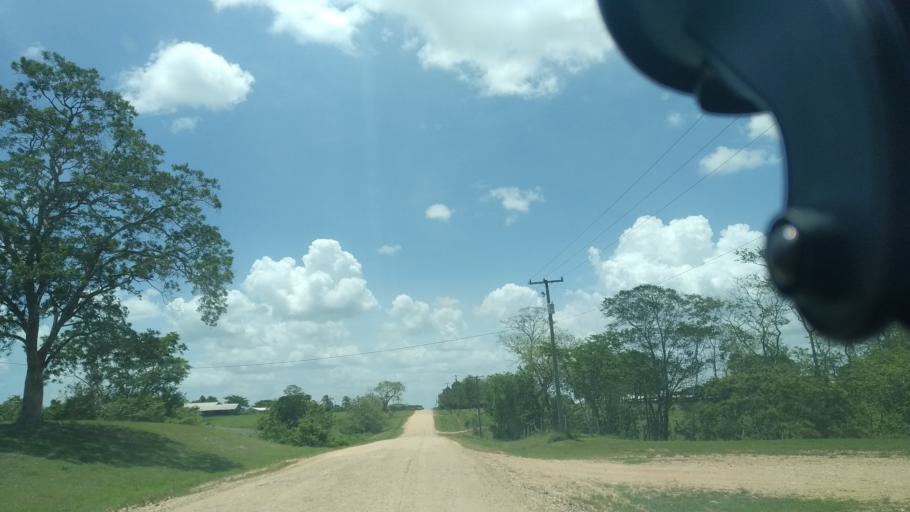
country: BZ
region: Cayo
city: San Ignacio
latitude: 17.2333
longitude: -88.9876
